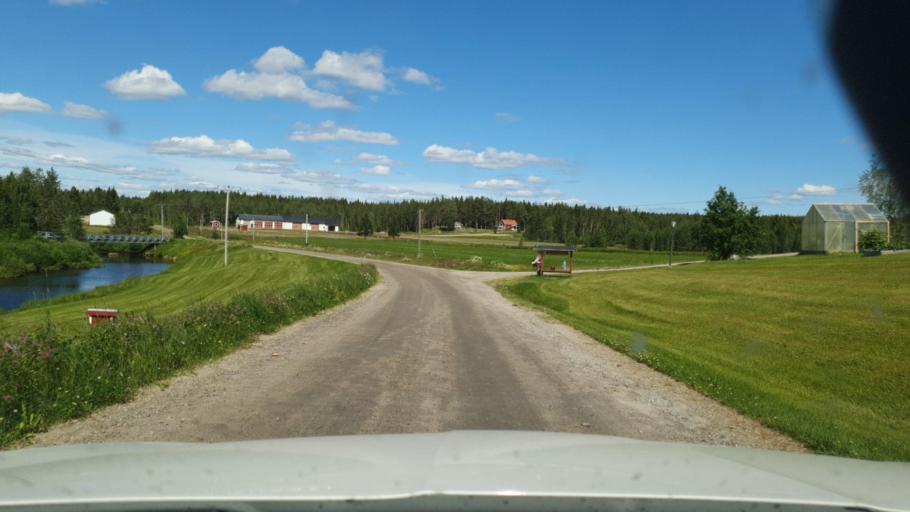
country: SE
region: Vaesterbotten
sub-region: Skelleftea Kommun
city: Backa
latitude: 65.1476
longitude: 21.1670
